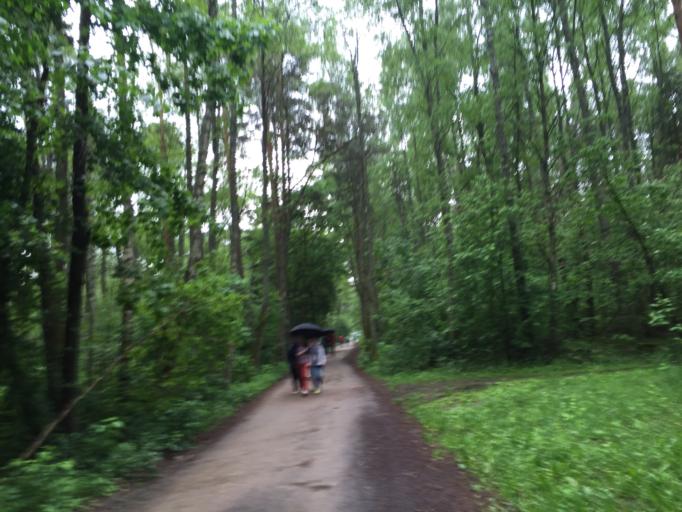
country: LT
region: Klaipedos apskritis
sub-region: Klaipeda
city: Klaipeda
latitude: 55.7975
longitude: 21.0716
